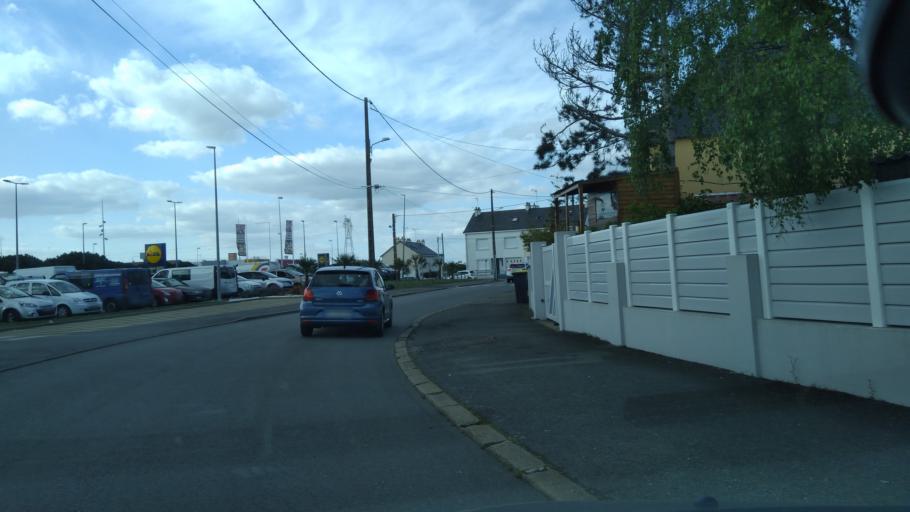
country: FR
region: Pays de la Loire
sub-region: Departement de la Loire-Atlantique
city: Saint-Nazaire
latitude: 47.2897
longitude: -2.2082
